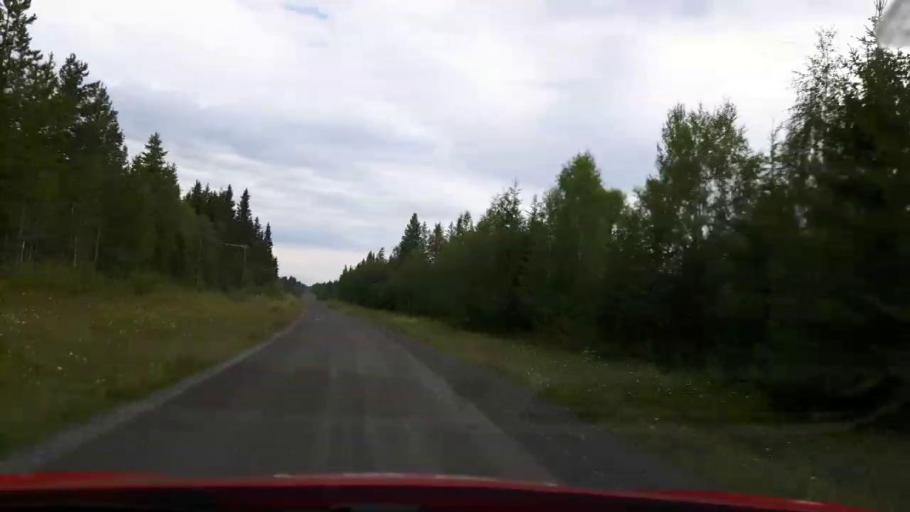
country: SE
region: Jaemtland
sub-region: Stroemsunds Kommun
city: Stroemsund
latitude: 63.5004
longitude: 15.3297
